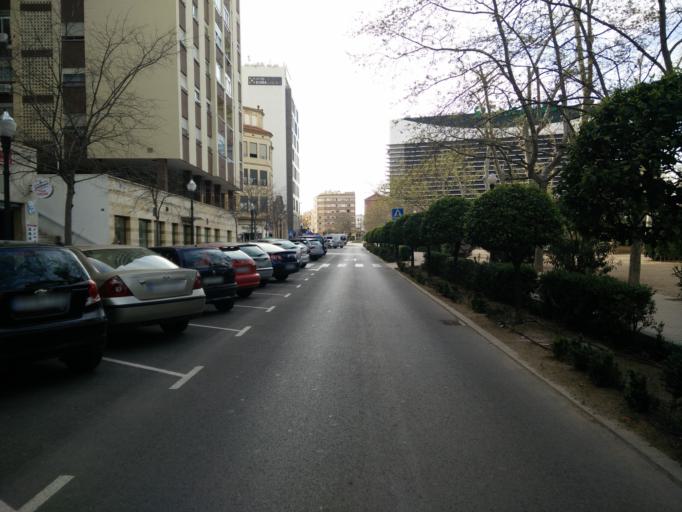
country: ES
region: Valencia
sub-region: Provincia de Castello
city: Castello de la Plana
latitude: 39.9866
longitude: -0.0460
